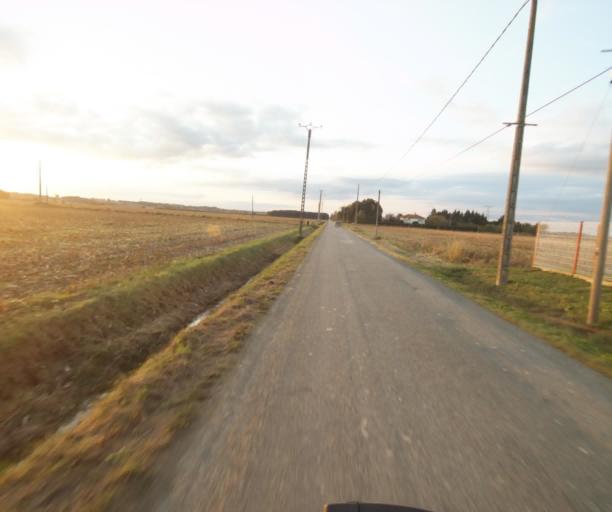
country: FR
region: Midi-Pyrenees
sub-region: Departement du Tarn-et-Garonne
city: Verdun-sur-Garonne
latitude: 43.8228
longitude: 1.2405
